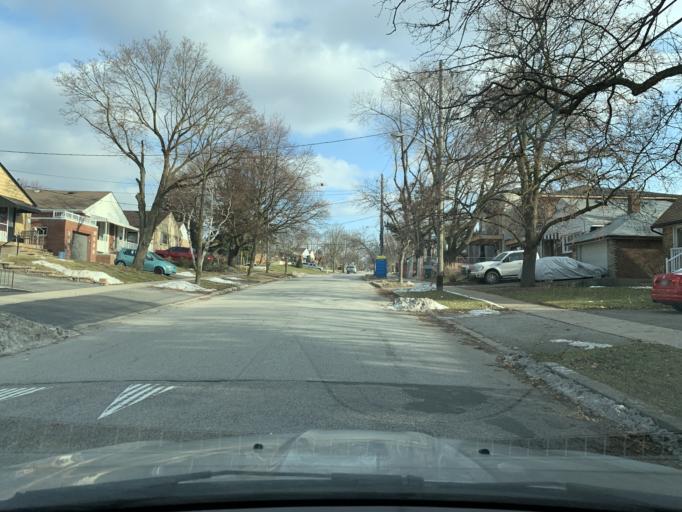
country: CA
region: Ontario
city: Toronto
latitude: 43.7038
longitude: -79.4842
